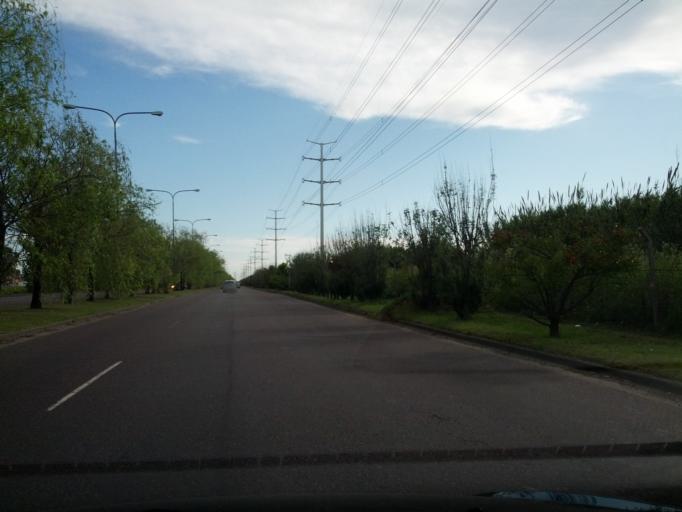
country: AR
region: Buenos Aires F.D.
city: Villa Lugano
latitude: -34.6921
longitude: -58.4505
